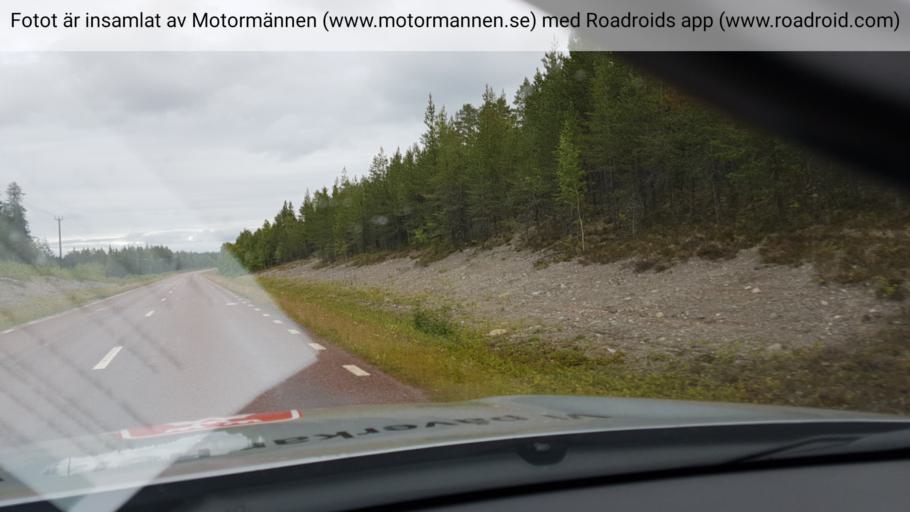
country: SE
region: Norrbotten
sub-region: Pajala Kommun
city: Pajala
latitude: 67.1266
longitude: 22.6073
